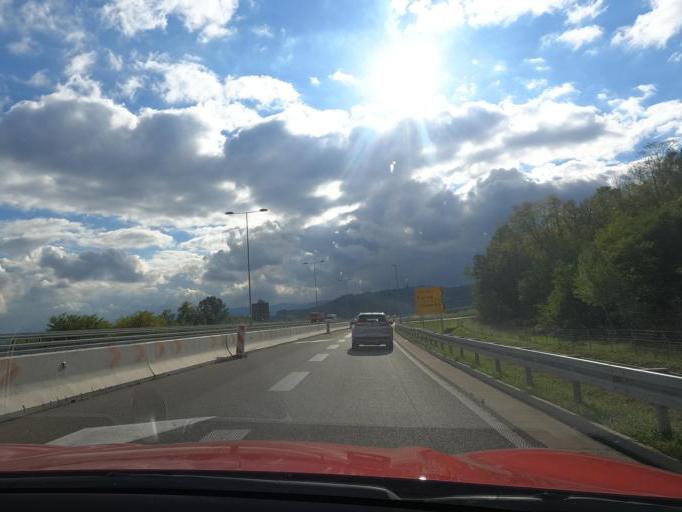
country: RS
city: Prislonica
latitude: 43.9240
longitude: 20.4015
